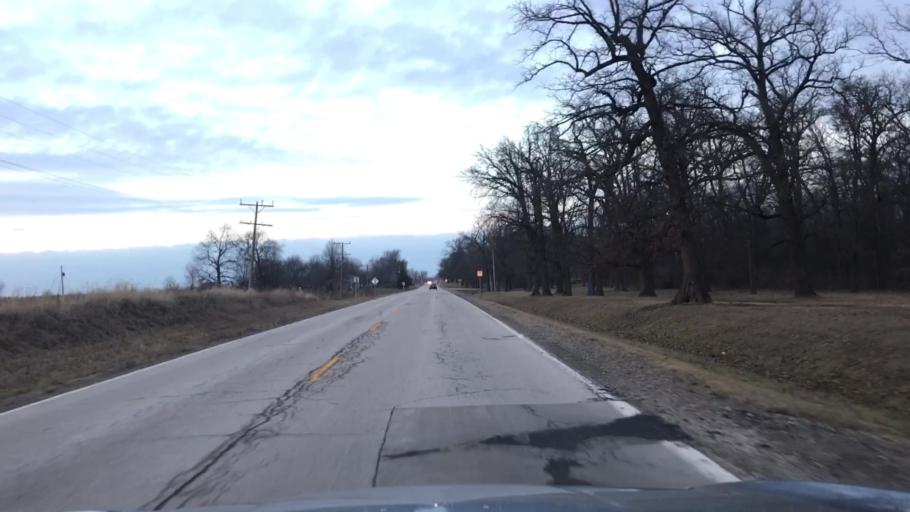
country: US
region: Illinois
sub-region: McLean County
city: Hudson
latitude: 40.6505
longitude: -88.9368
